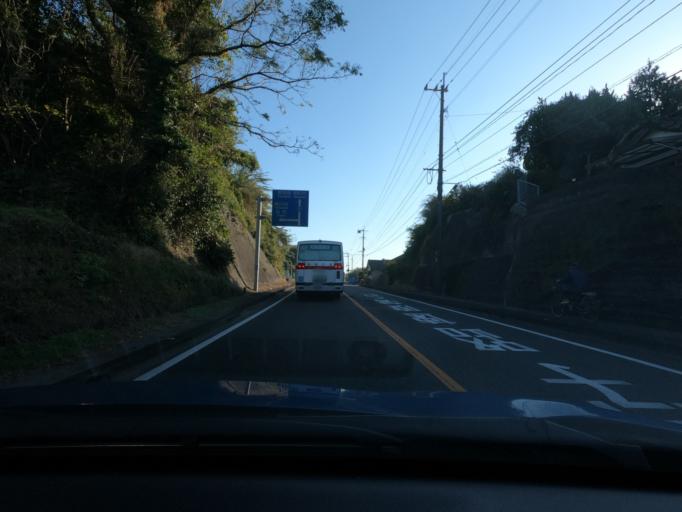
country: JP
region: Kagoshima
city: Akune
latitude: 31.9850
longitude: 130.2039
